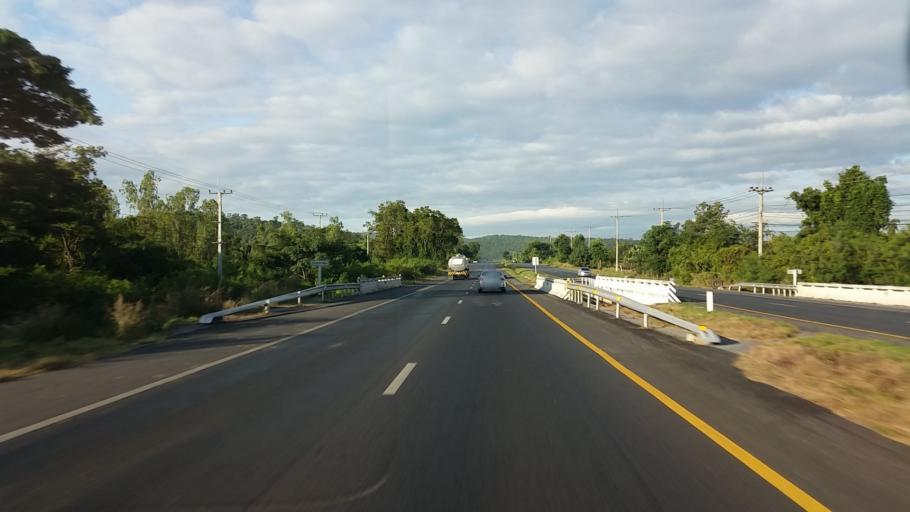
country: TH
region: Lop Buri
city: Phatthana Nikhom
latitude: 14.9847
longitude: 100.9220
